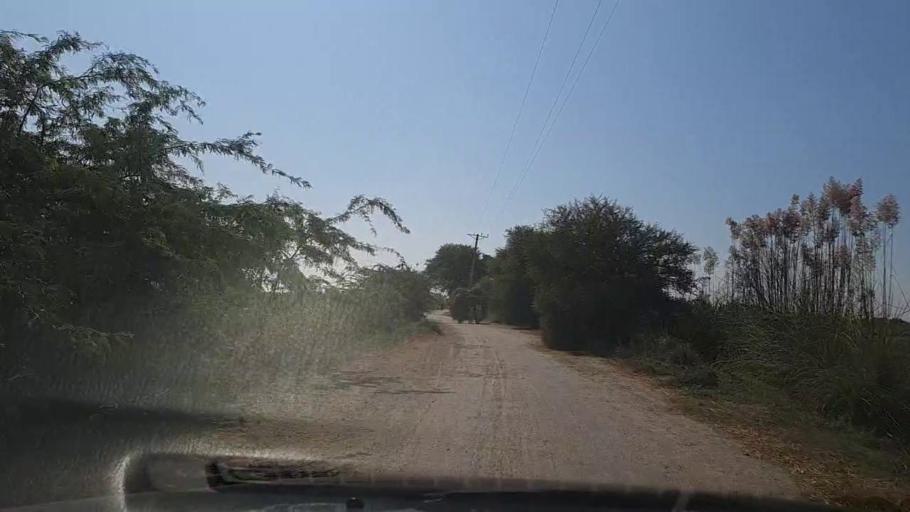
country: PK
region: Sindh
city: Mirpur Sakro
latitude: 24.6036
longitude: 67.7884
